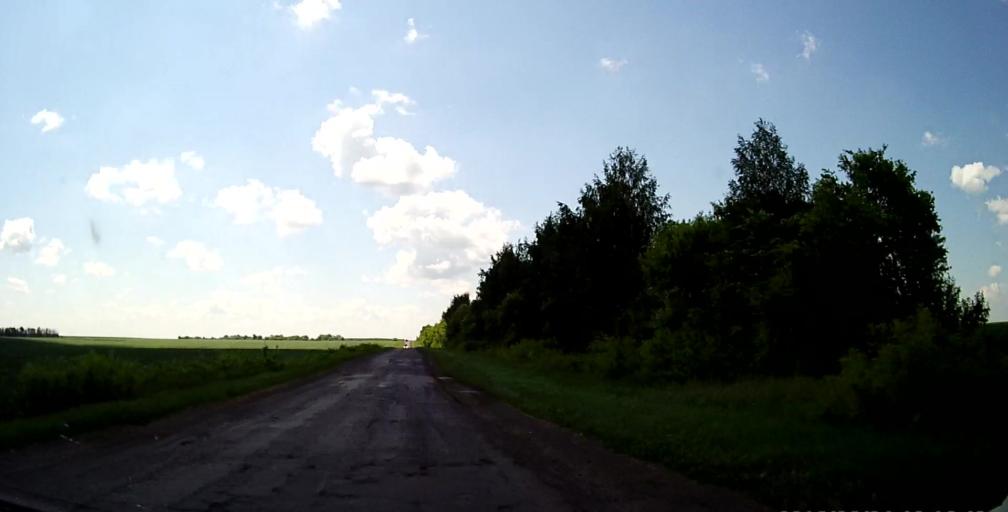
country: RU
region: Lipetsk
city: Chaplygin
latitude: 53.2835
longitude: 39.9606
